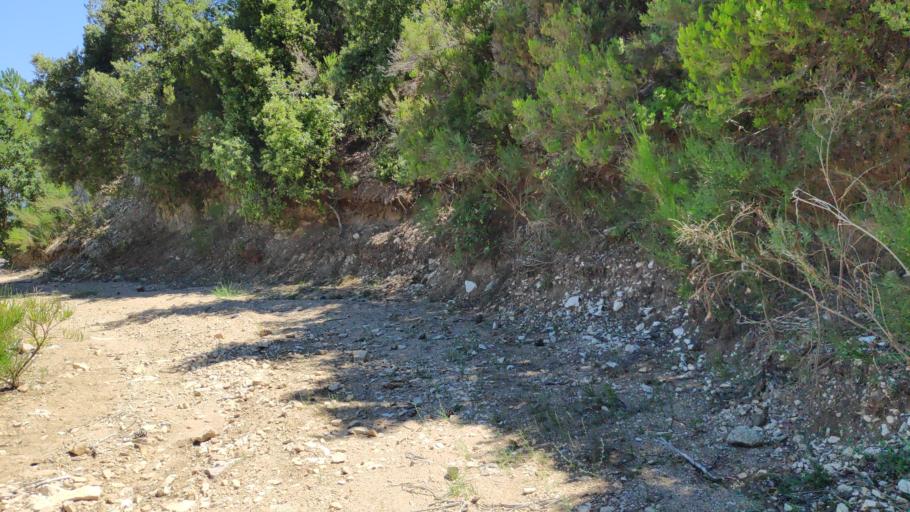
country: IT
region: Calabria
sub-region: Provincia di Reggio Calabria
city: Pazzano
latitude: 38.4776
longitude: 16.3982
